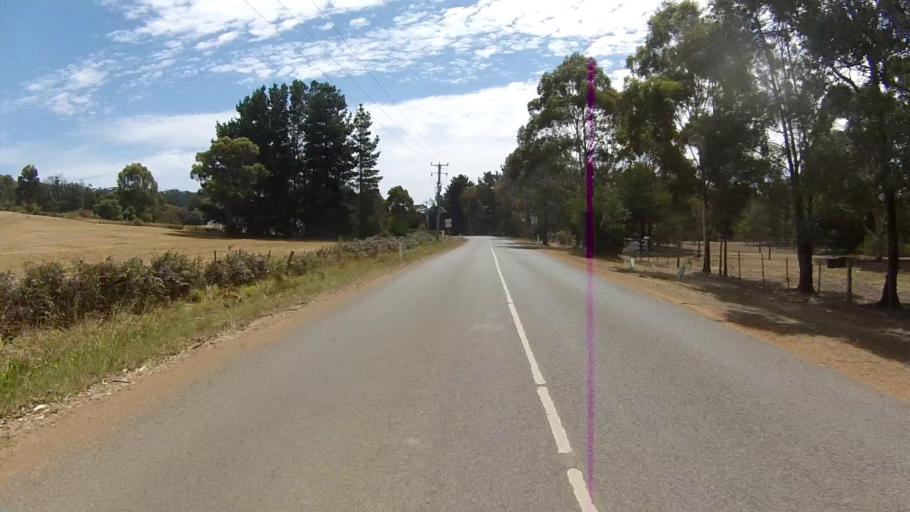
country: AU
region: Tasmania
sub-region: Clarence
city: Sandford
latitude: -42.9863
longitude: 147.5176
